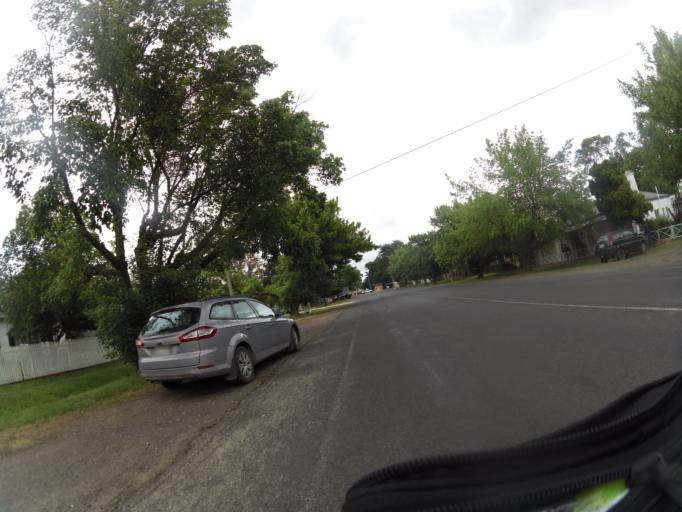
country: AU
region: Victoria
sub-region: Mount Alexander
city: Castlemaine
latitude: -37.0675
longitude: 144.2122
